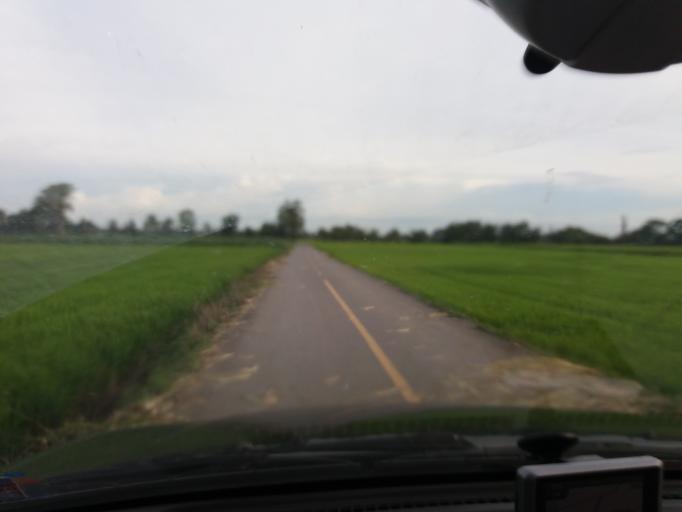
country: TH
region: Suphan Buri
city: Doembang Nangbuat
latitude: 14.8300
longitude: 100.1425
